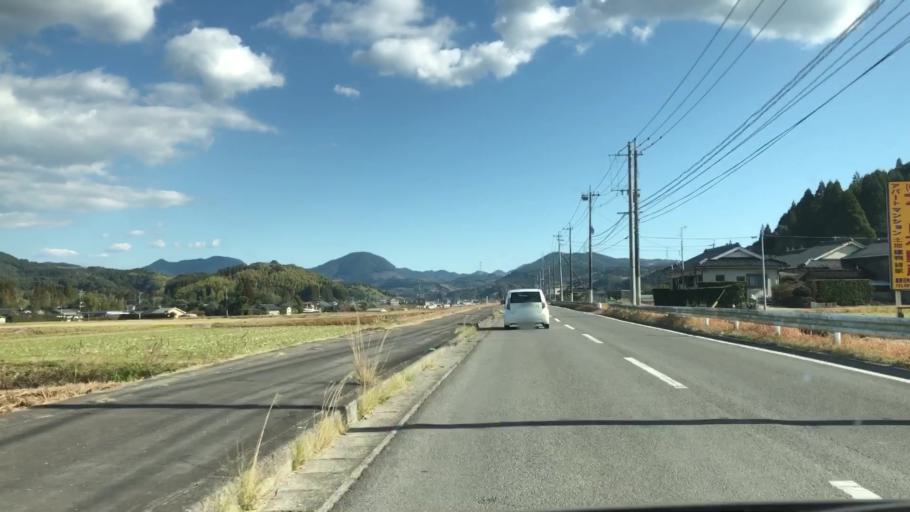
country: JP
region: Kagoshima
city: Satsumasendai
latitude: 31.7977
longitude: 130.4338
